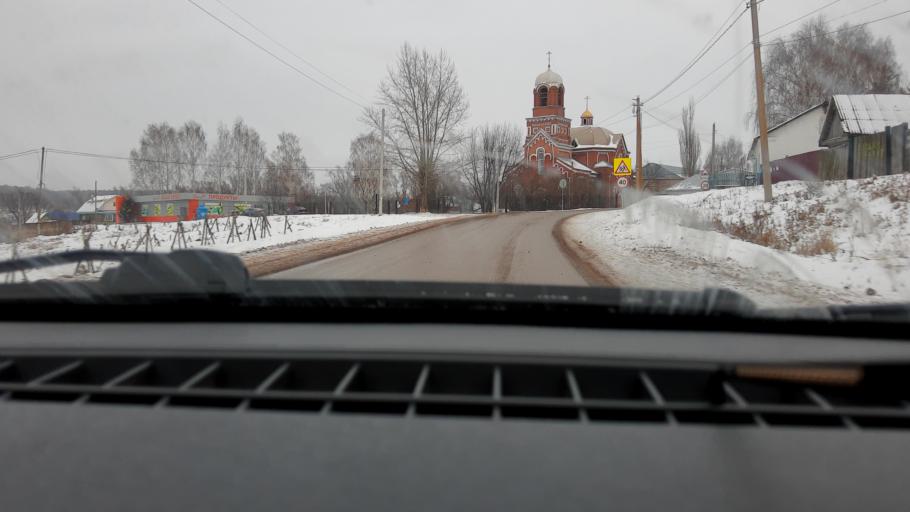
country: RU
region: Bashkortostan
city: Kabakovo
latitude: 54.7036
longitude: 56.2486
